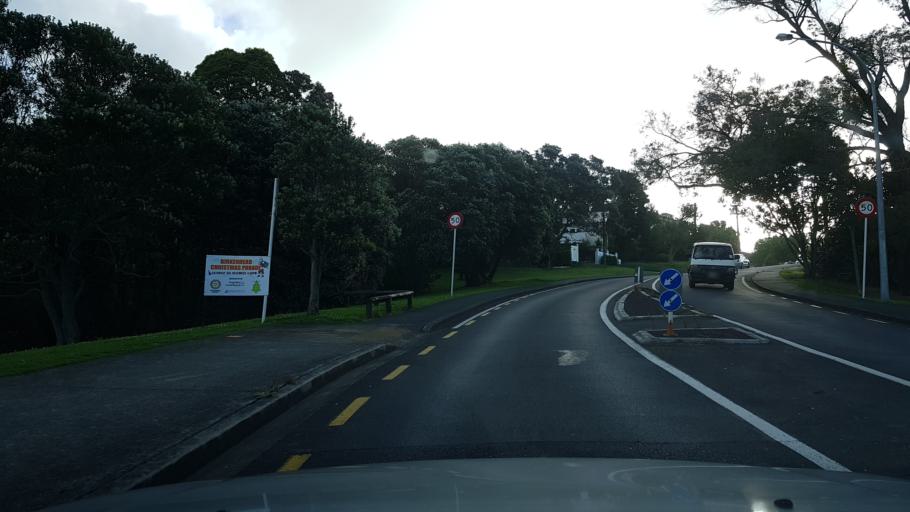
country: NZ
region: Auckland
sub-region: Auckland
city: North Shore
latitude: -36.8163
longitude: 174.7392
